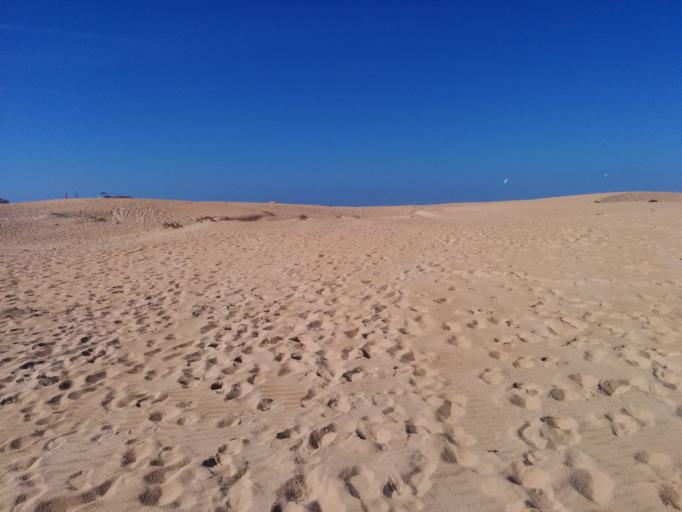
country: PT
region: Faro
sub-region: Vila do Bispo
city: Vila do Bispo
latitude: 37.1961
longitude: -8.9019
